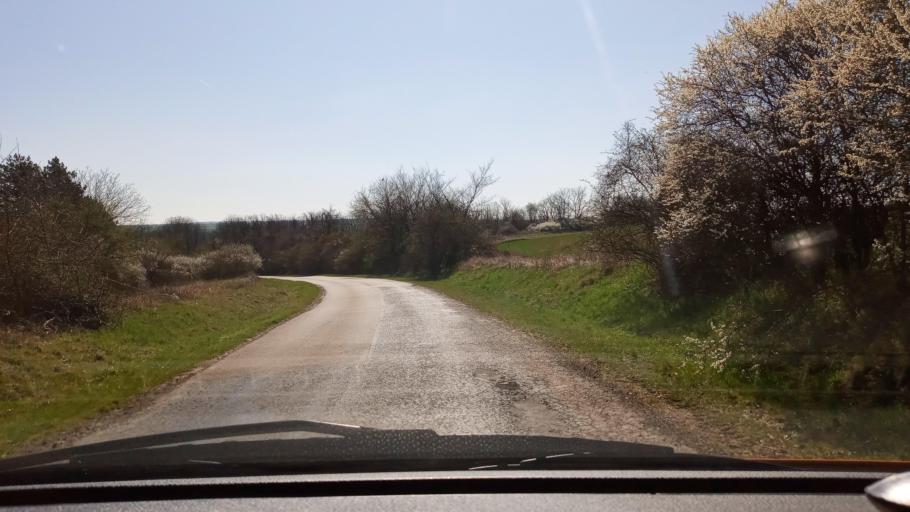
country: HU
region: Baranya
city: Kozarmisleny
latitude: 46.0736
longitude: 18.3579
